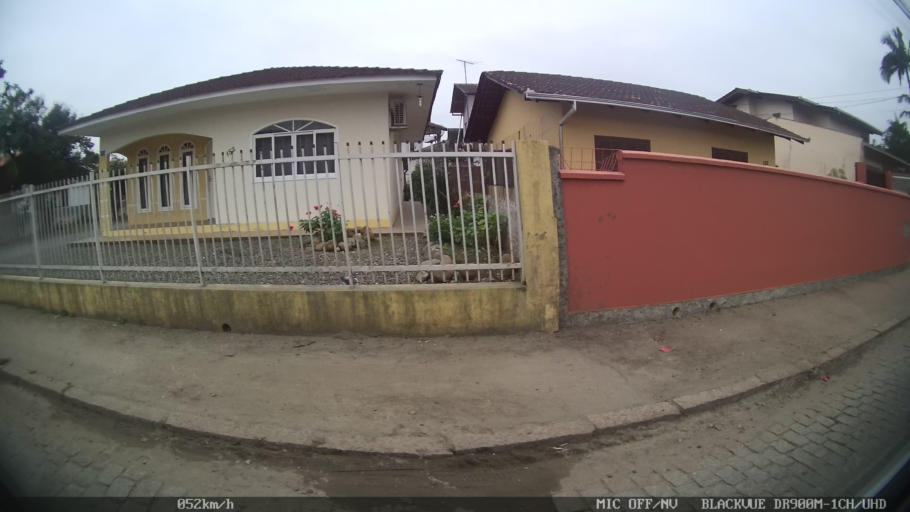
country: BR
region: Santa Catarina
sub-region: Joinville
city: Joinville
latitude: -26.3430
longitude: -48.8492
